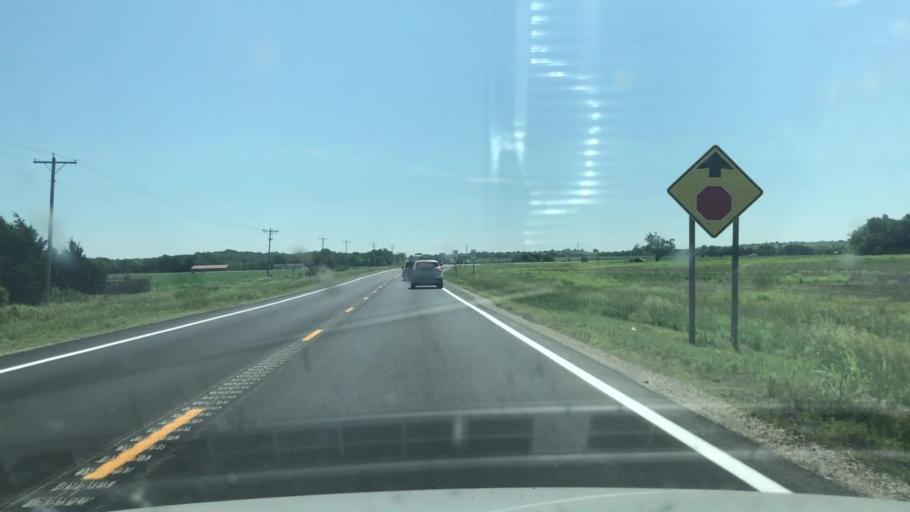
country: US
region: Kansas
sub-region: Butler County
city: Douglass
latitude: 37.3901
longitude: -97.0109
